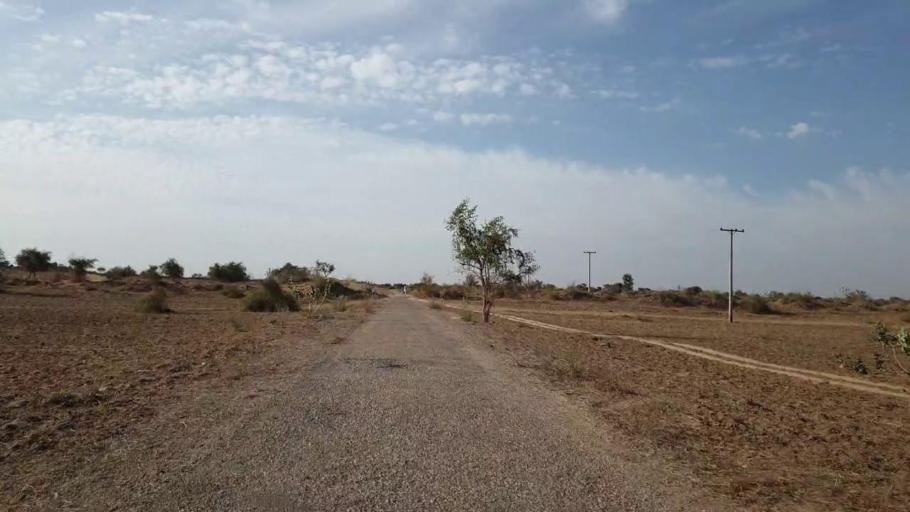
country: PK
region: Sindh
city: Nabisar
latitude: 25.0498
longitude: 69.9702
